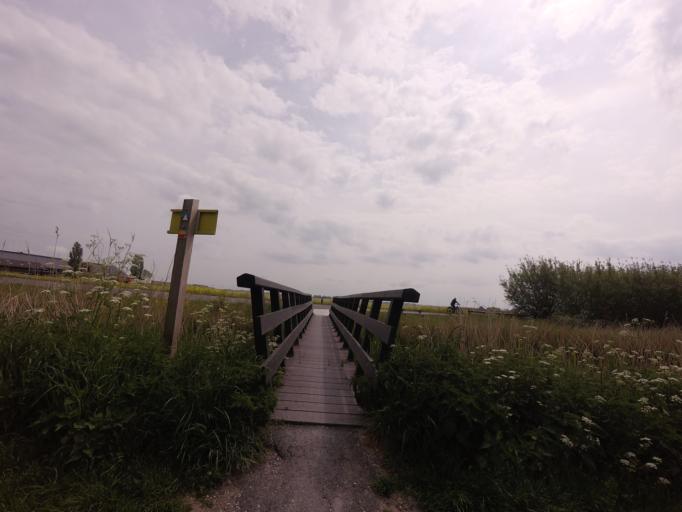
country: NL
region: Friesland
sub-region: Sudwest Fryslan
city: Bolsward
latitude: 53.0953
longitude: 5.4772
